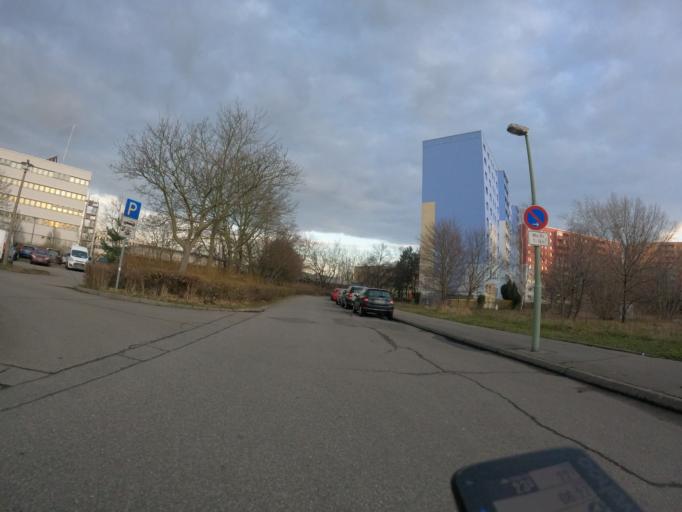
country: DE
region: Berlin
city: Biesdorf
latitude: 52.5350
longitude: 13.5399
